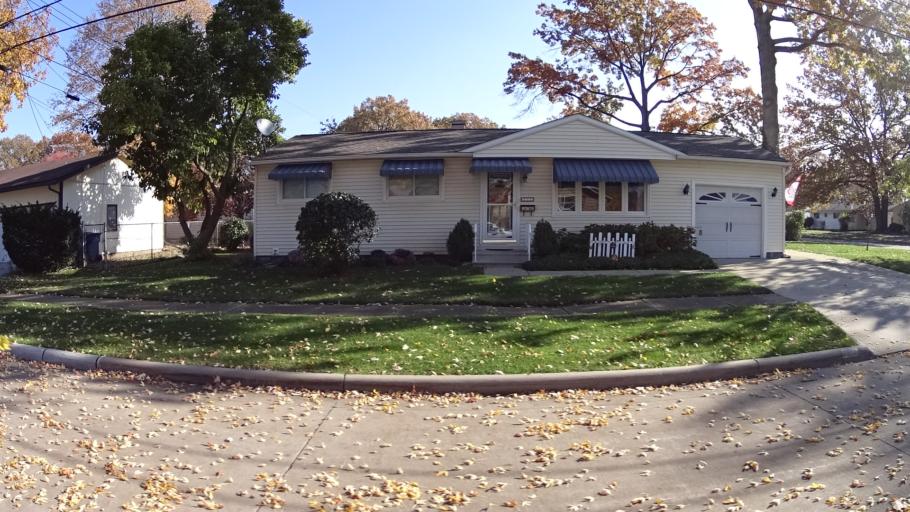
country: US
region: Ohio
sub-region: Lorain County
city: Lorain
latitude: 41.4707
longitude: -82.1440
